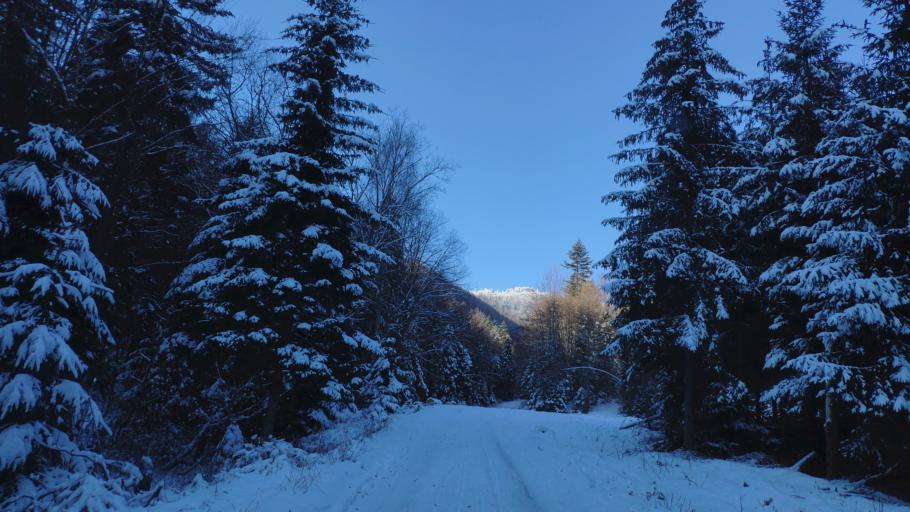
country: SK
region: Kosicky
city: Medzev
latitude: 48.7639
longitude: 20.9660
